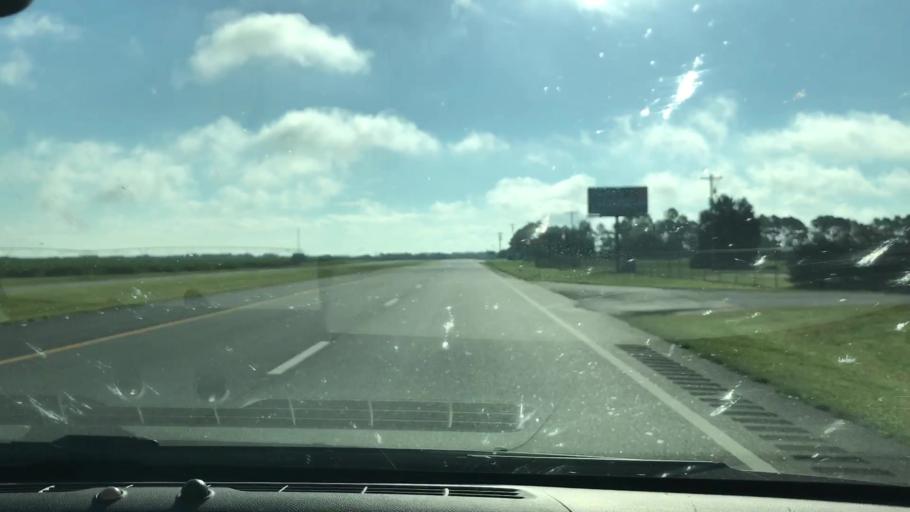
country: US
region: Georgia
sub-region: Terrell County
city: Dawson
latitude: 31.7350
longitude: -84.3990
